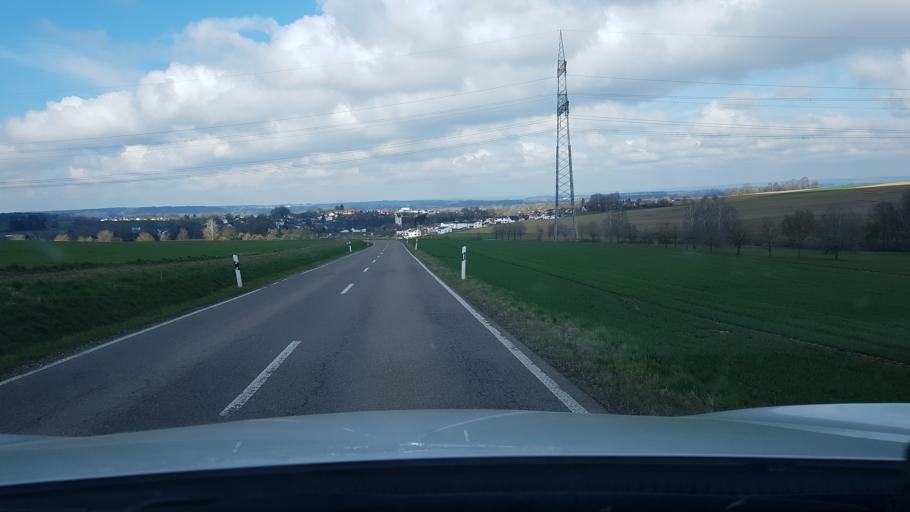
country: DE
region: Baden-Wuerttemberg
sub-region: Tuebingen Region
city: Maselheim
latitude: 48.1537
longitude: 9.8845
